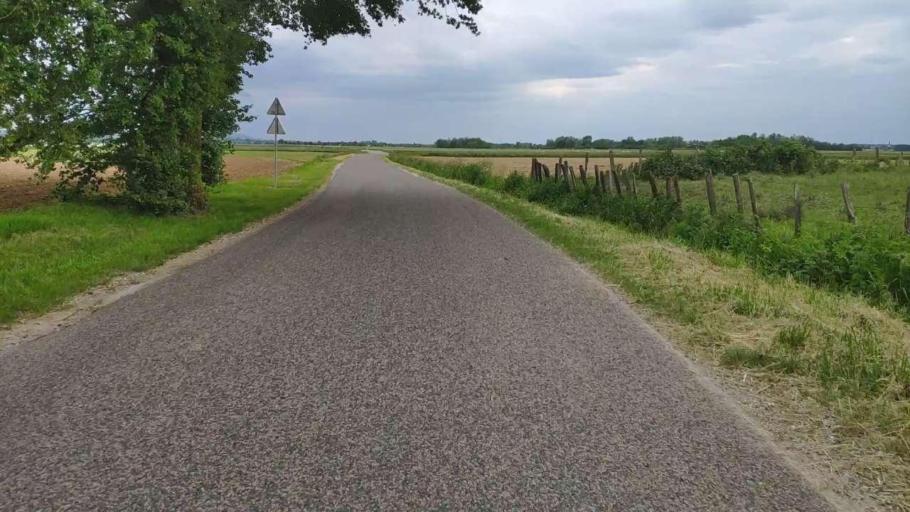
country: FR
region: Franche-Comte
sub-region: Departement du Jura
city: Bletterans
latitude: 46.7759
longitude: 5.5057
